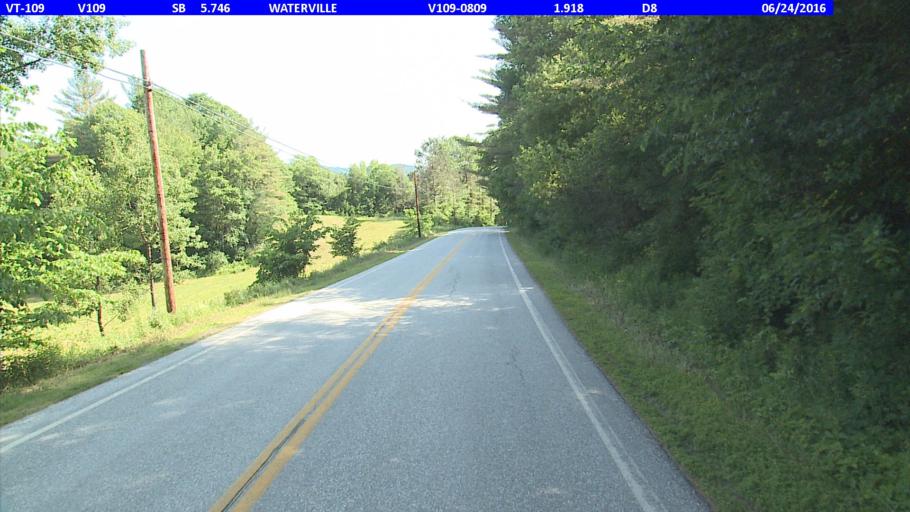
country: US
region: Vermont
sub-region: Lamoille County
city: Johnson
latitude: 44.7075
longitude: -72.7596
